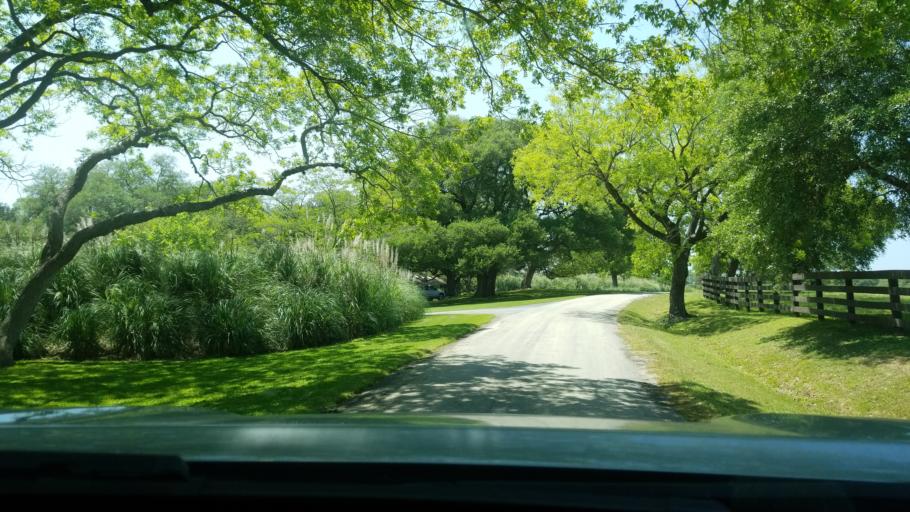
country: US
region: Texas
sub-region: Blanco County
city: Blanco
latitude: 30.0056
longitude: -98.4348
